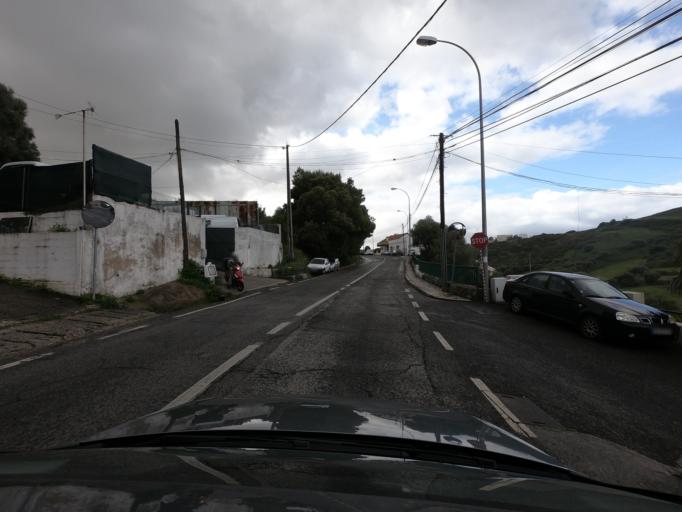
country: PT
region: Lisbon
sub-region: Oeiras
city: Quejas
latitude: 38.7333
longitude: -9.2597
